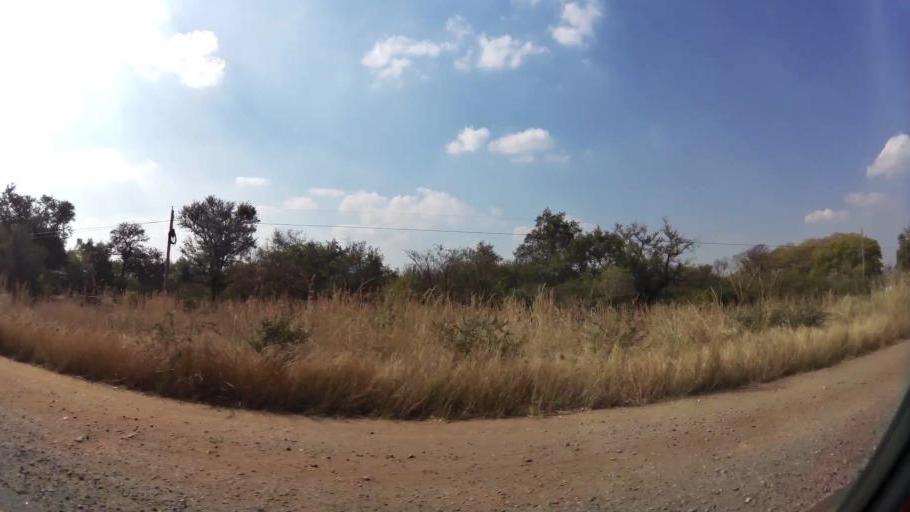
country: ZA
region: North-West
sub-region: Bojanala Platinum District Municipality
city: Rustenburg
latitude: -25.5463
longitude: 27.1278
